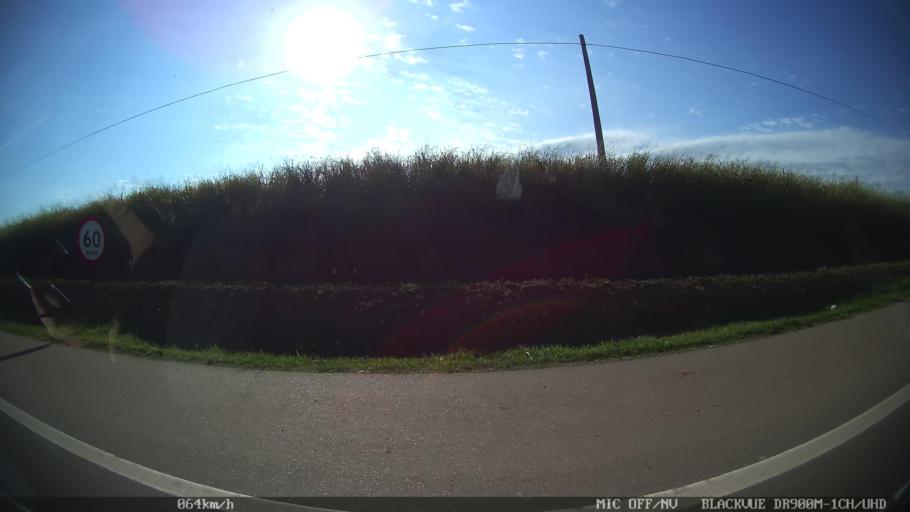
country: BR
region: Sao Paulo
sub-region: Piracicaba
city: Piracicaba
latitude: -22.6621
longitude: -47.6122
